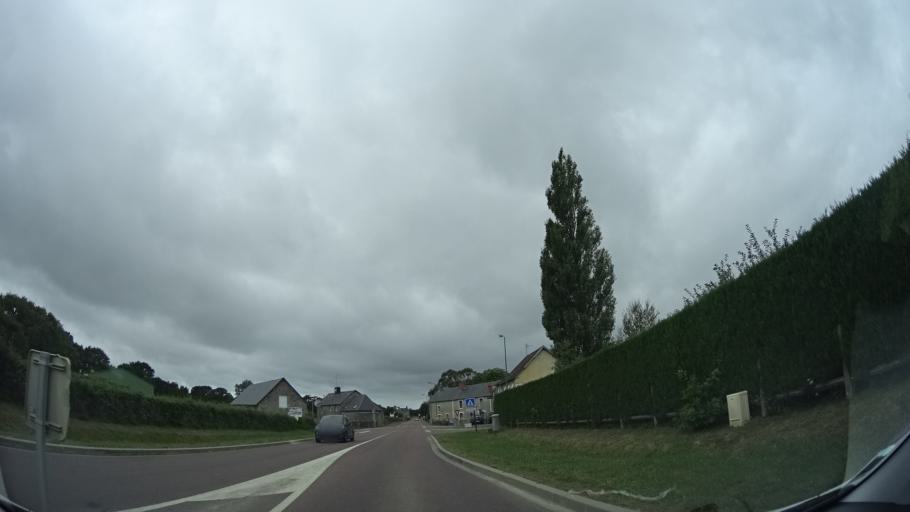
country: FR
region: Lower Normandy
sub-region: Departement de la Manche
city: La Haye-du-Puits
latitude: 49.3002
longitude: -1.5714
